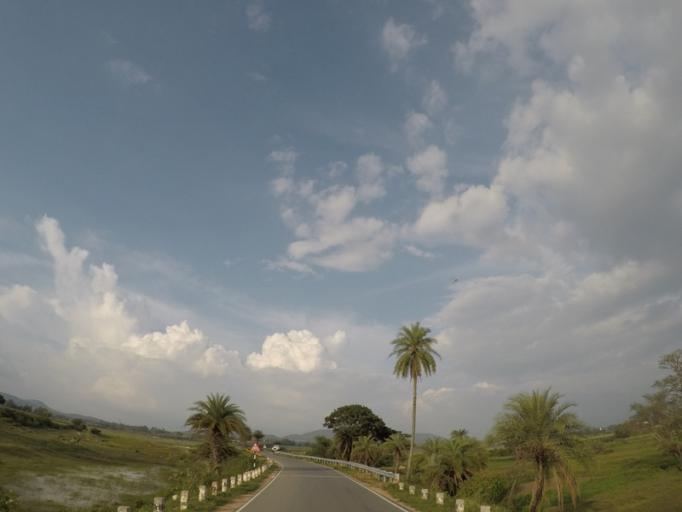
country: IN
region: Karnataka
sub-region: Chikmagalur
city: Chikmagalur
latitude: 13.2657
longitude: 75.8409
